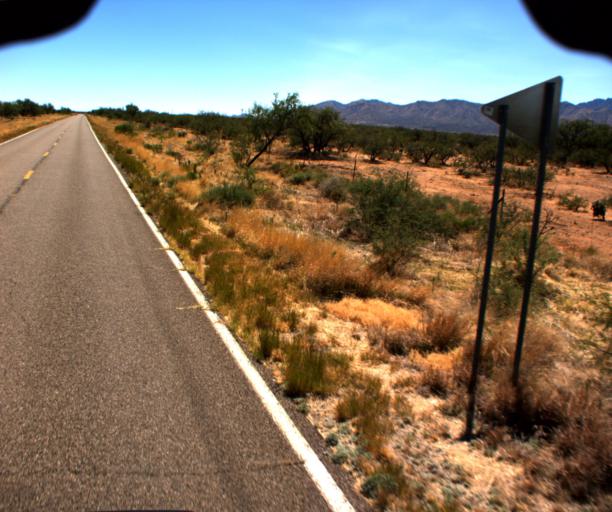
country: US
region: Arizona
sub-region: Pima County
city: Three Points
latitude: 31.8191
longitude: -111.4387
